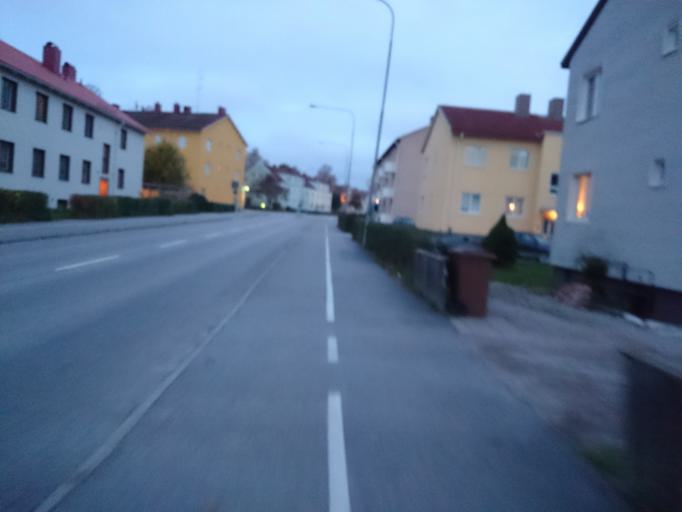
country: SE
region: Soedermanland
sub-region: Nykopings Kommun
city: Nykoping
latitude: 58.7537
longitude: 17.0267
